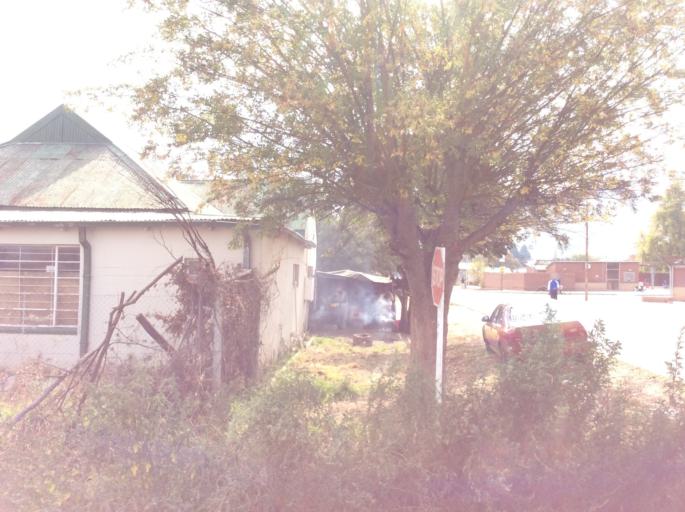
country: LS
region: Mafeteng
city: Mafeteng
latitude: -29.7304
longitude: 27.0365
